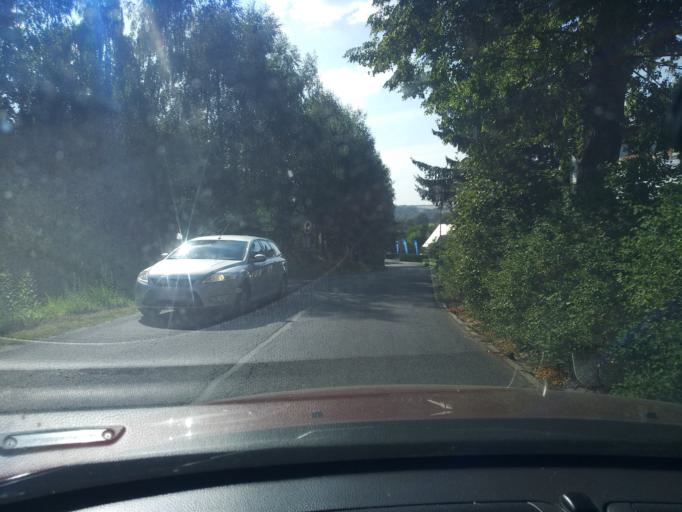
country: PL
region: Lower Silesian Voivodeship
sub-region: Powiat lubanski
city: Lesna
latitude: 51.0263
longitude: 15.2793
